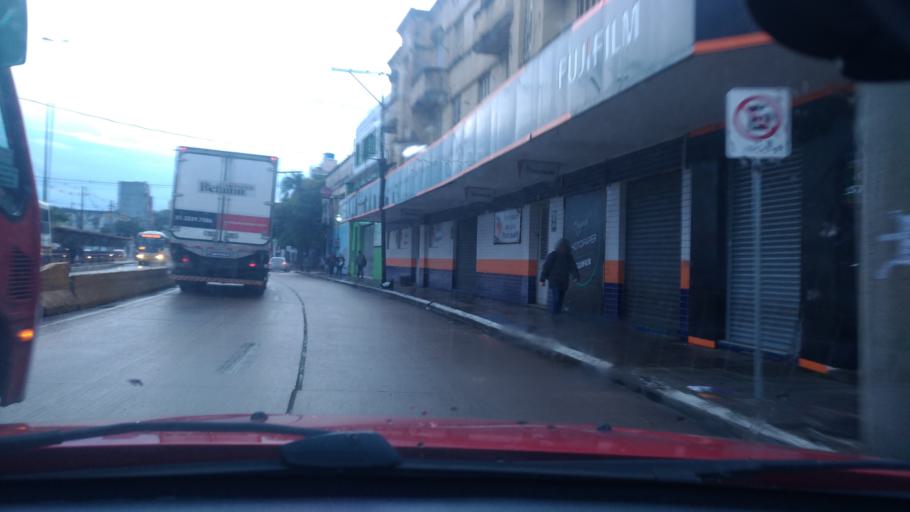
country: BR
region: Rio Grande do Sul
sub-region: Porto Alegre
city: Porto Alegre
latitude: -30.0213
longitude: -51.2113
